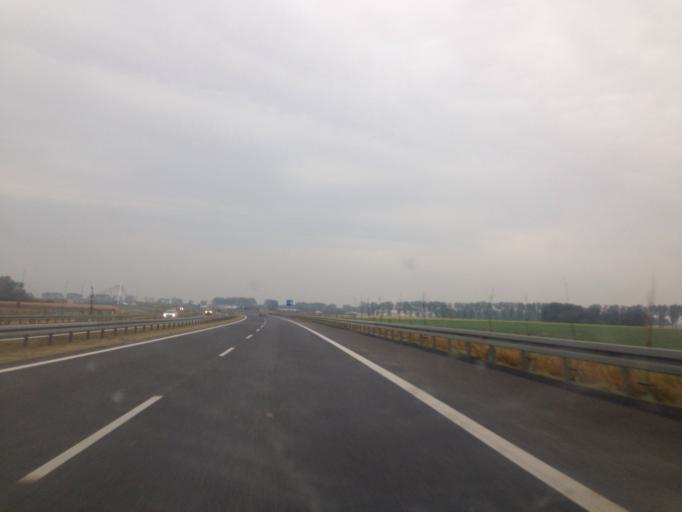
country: PL
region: Greater Poland Voivodeship
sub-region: Powiat poznanski
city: Kostrzyn
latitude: 52.3720
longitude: 17.2143
